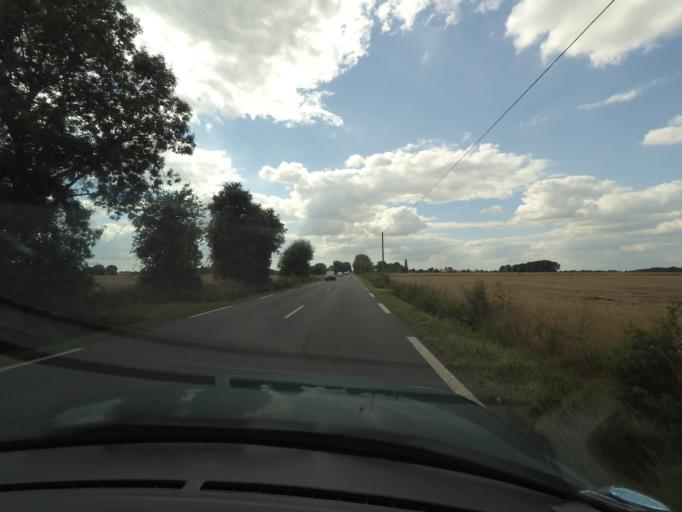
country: FR
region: Pays de la Loire
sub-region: Departement de la Vendee
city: Bouffere
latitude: 46.9728
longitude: -1.3808
